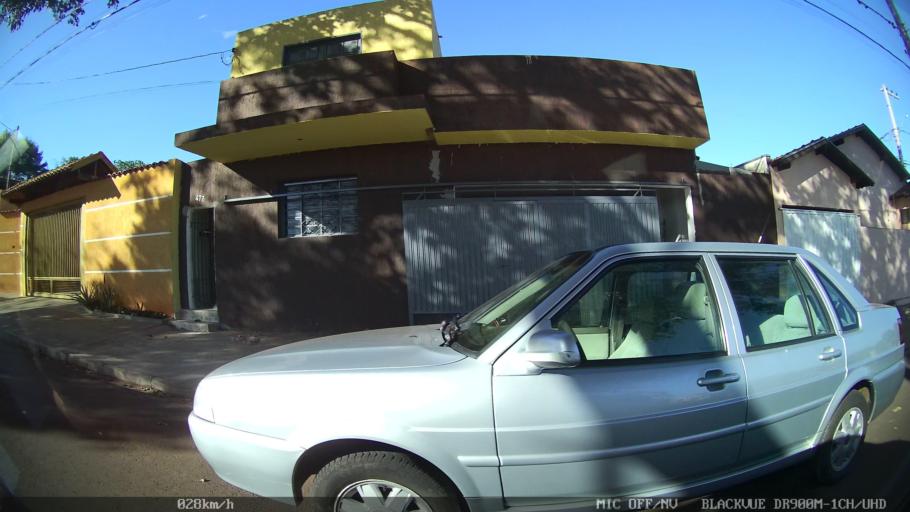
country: BR
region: Sao Paulo
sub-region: Olimpia
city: Olimpia
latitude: -20.7378
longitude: -48.9058
